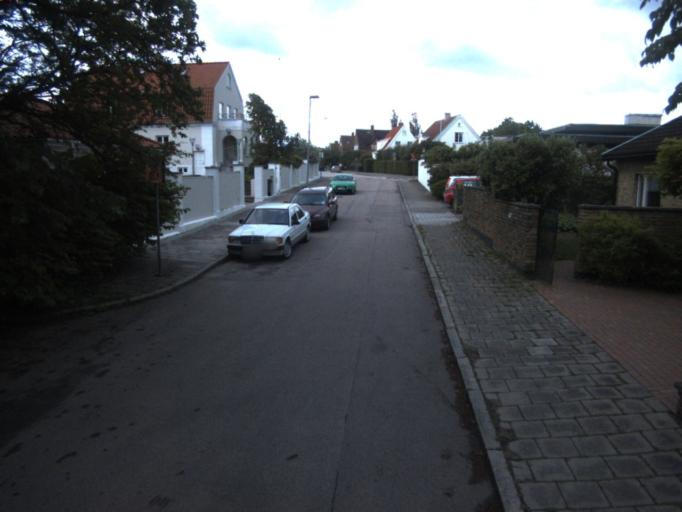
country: SE
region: Skane
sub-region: Helsingborg
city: Helsingborg
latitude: 56.0638
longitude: 12.6887
